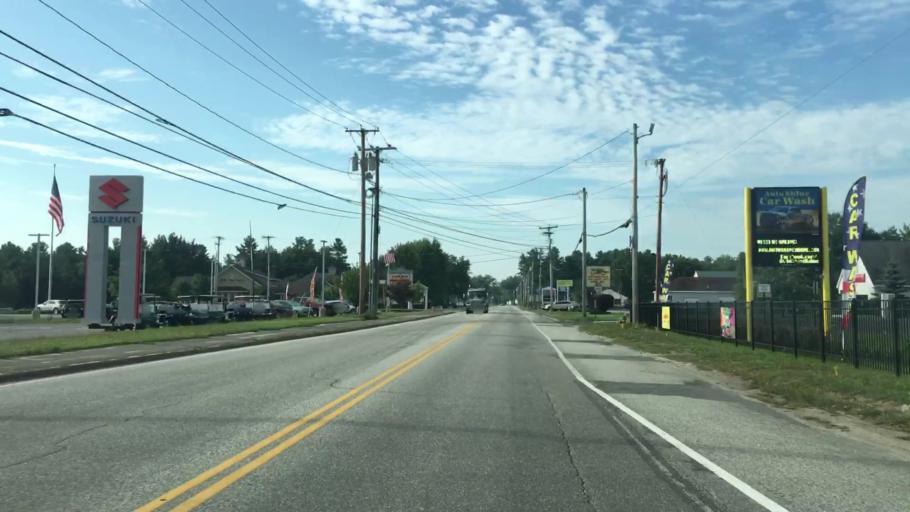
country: US
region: Maine
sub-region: Cumberland County
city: North Windham
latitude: 43.8262
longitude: -70.4346
